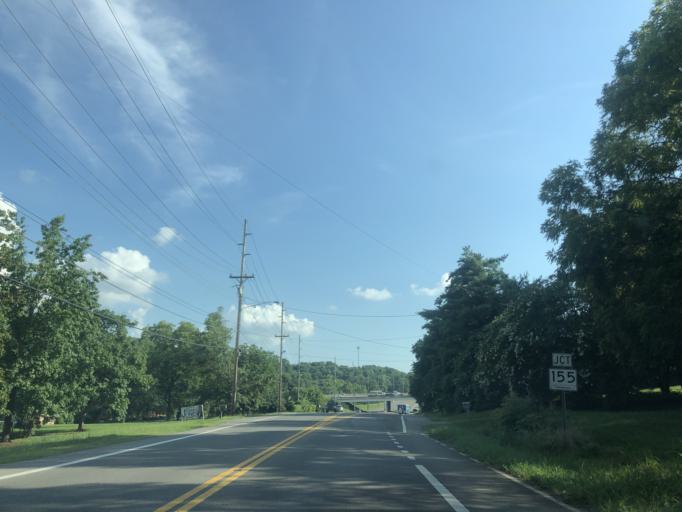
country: US
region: Tennessee
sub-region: Davidson County
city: Nashville
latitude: 36.2320
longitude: -86.8326
